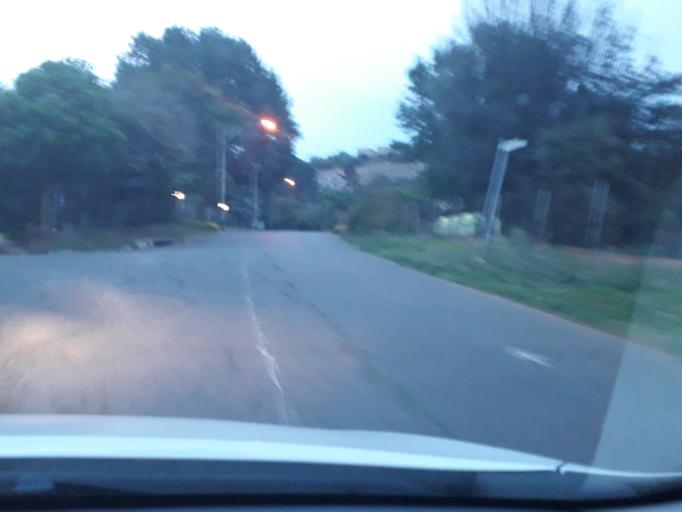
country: ZA
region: Gauteng
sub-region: City of Johannesburg Metropolitan Municipality
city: Johannesburg
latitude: -26.1527
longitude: 27.9772
